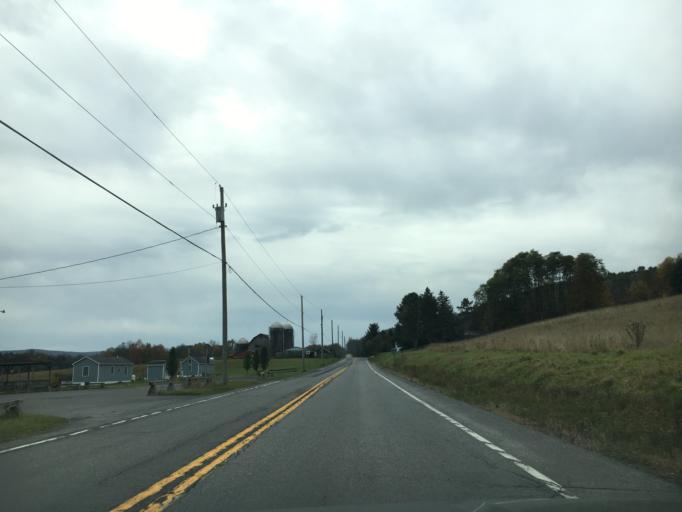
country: US
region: New York
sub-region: Otsego County
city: Cooperstown
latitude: 42.6268
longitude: -74.9625
